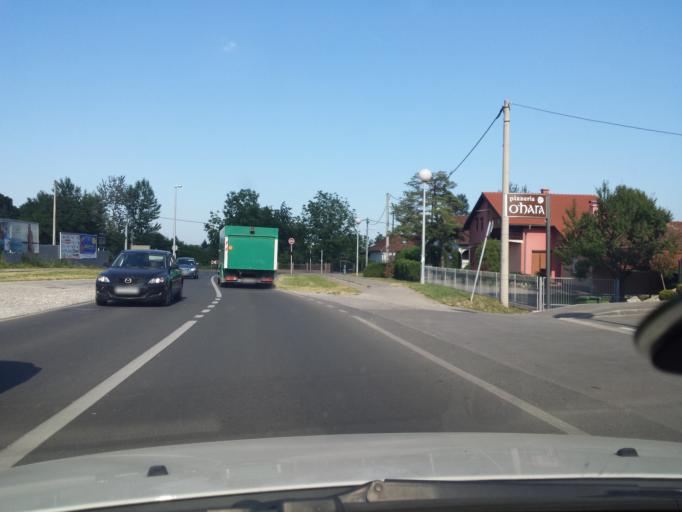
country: HR
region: Grad Zagreb
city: Jankomir
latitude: 45.8064
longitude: 15.9071
